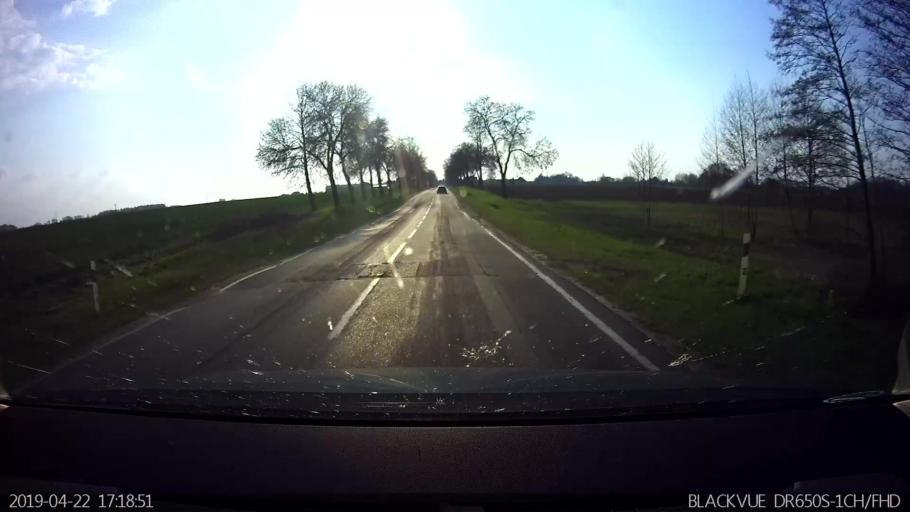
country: PL
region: Masovian Voivodeship
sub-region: Powiat sokolowski
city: Repki
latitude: 52.3849
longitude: 22.4053
